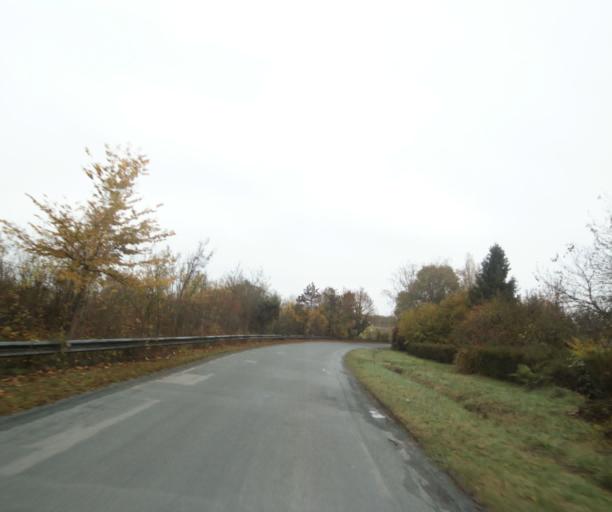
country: FR
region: Poitou-Charentes
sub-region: Departement de la Charente-Maritime
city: Saintes
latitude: 45.7543
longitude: -0.6685
